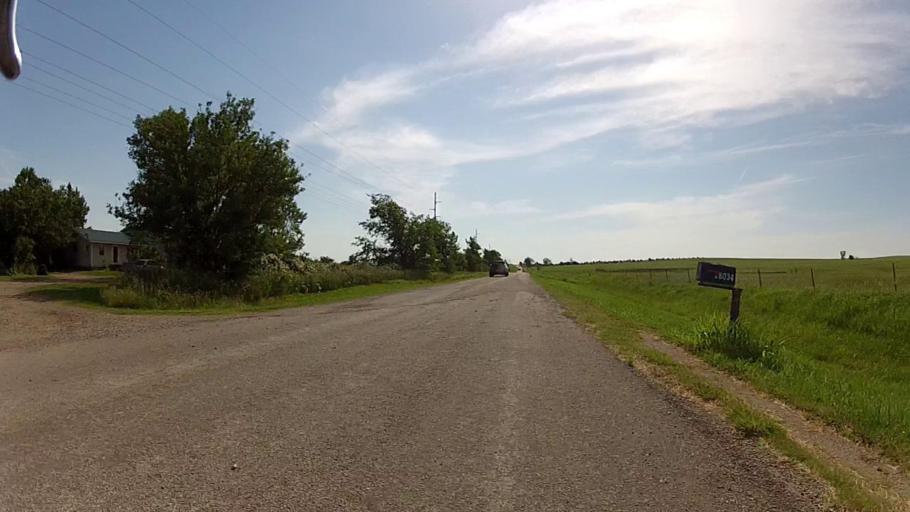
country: US
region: Kansas
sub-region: Cowley County
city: Winfield
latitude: 37.0710
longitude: -96.6615
